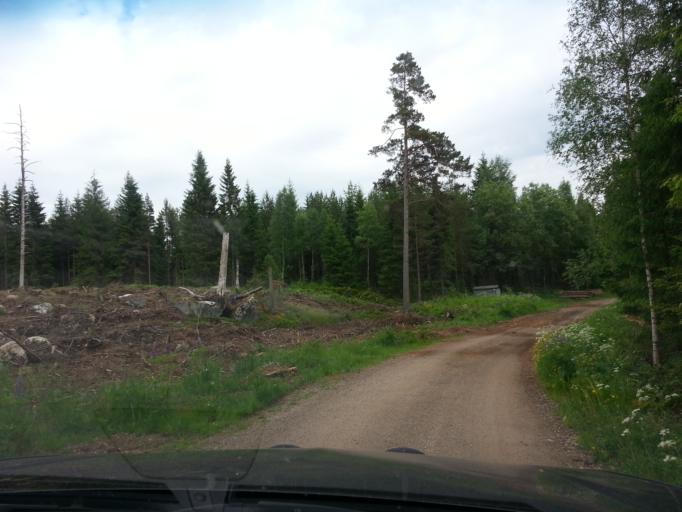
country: SE
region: Joenkoeping
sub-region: Vetlanda Kommun
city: Vetlanda
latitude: 57.2886
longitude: 15.1281
